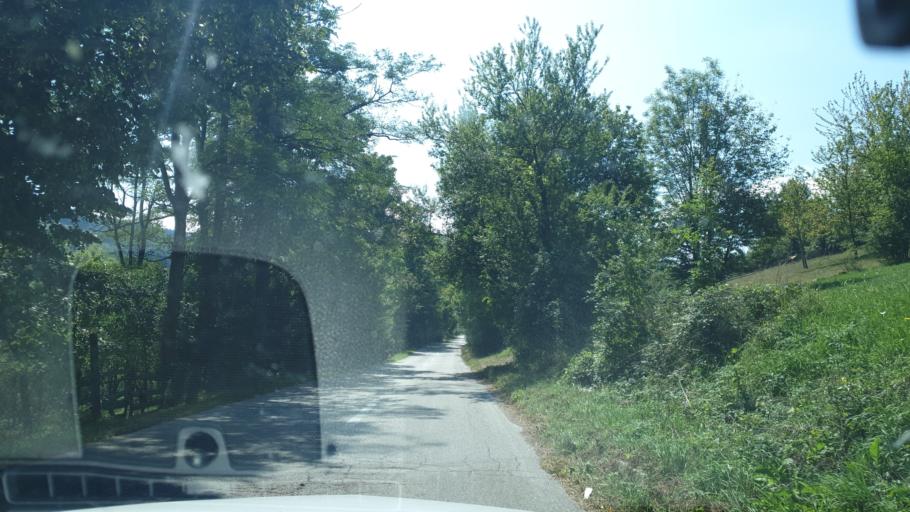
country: RS
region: Central Serbia
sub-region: Zlatiborski Okrug
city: Cajetina
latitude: 43.6864
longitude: 19.8479
